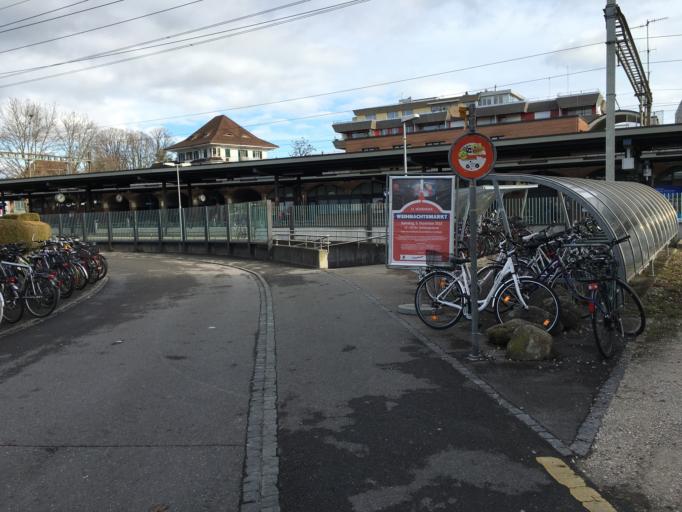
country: CH
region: Bern
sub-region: Bern-Mittelland District
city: Munsingen
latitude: 46.8732
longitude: 7.5589
